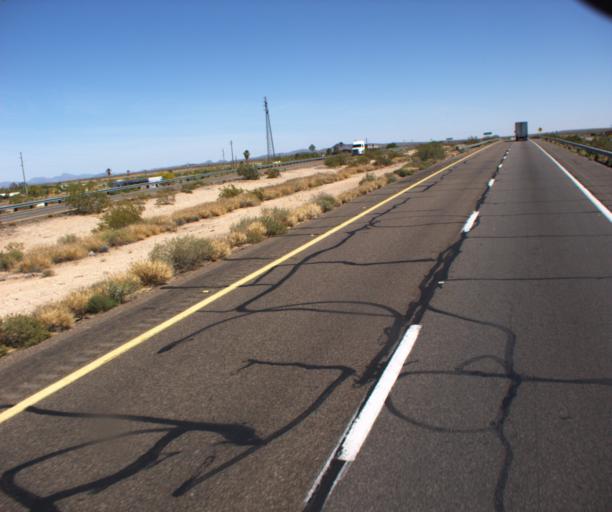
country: US
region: Arizona
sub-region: Maricopa County
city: Gila Bend
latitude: 32.8580
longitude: -113.2154
